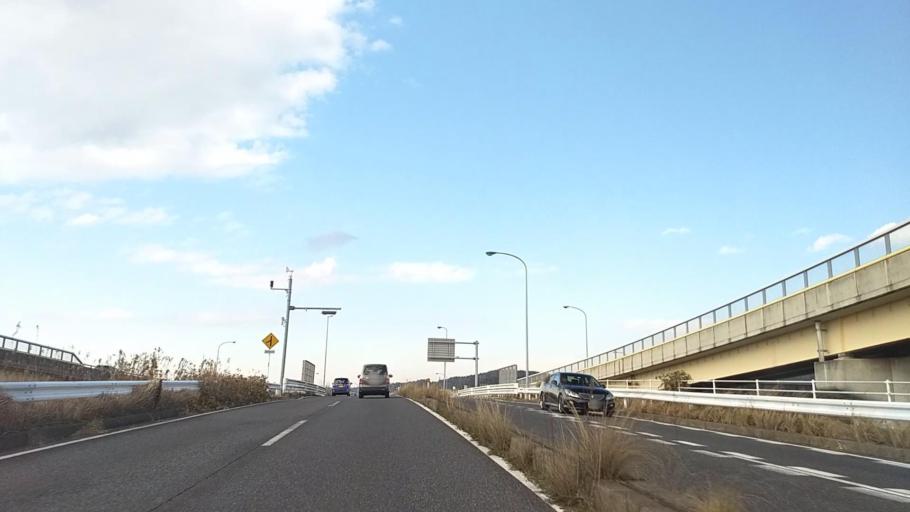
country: JP
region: Chiba
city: Togane
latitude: 35.5514
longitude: 140.3492
